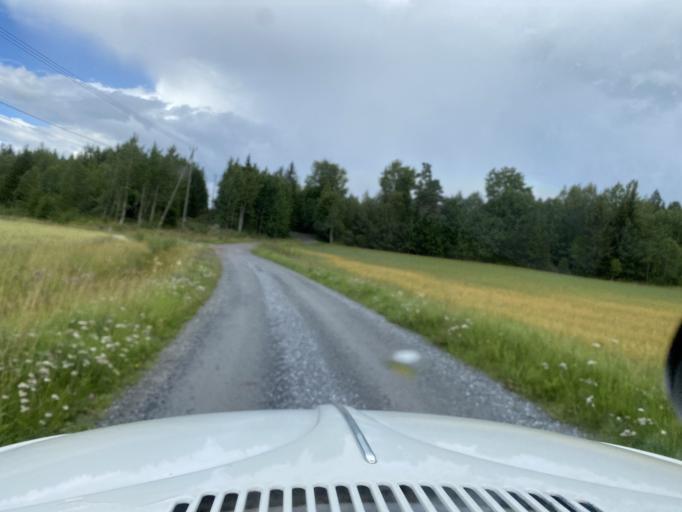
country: FI
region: Pirkanmaa
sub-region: Lounais-Pirkanmaa
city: Punkalaidun
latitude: 61.1261
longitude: 23.0635
